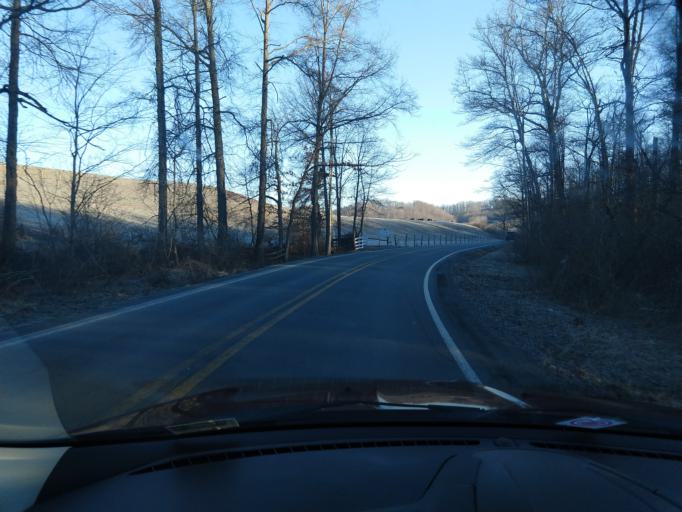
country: US
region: West Virginia
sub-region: Greenbrier County
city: Rainelle
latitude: 37.8615
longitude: -80.7193
